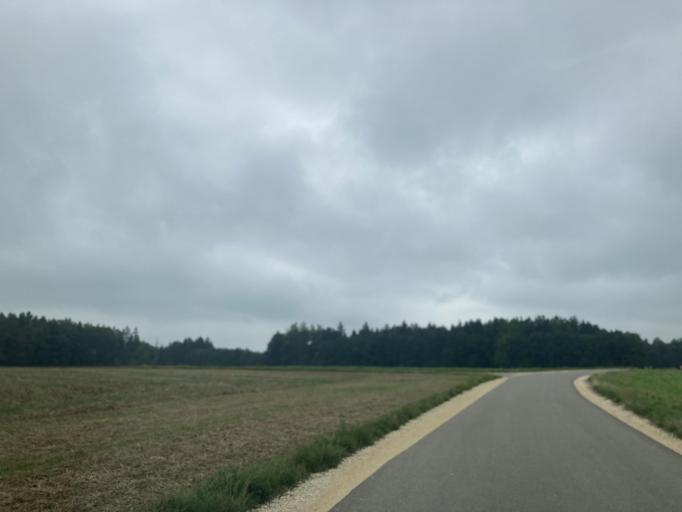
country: DE
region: Bavaria
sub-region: Swabia
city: Medlingen
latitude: 48.5799
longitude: 10.3090
